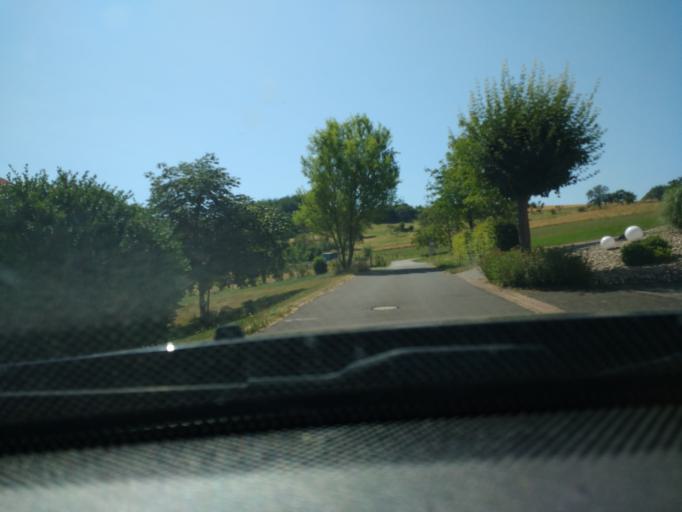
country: DE
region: Rheinland-Pfalz
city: Flussbach
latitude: 50.0153
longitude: 6.9280
